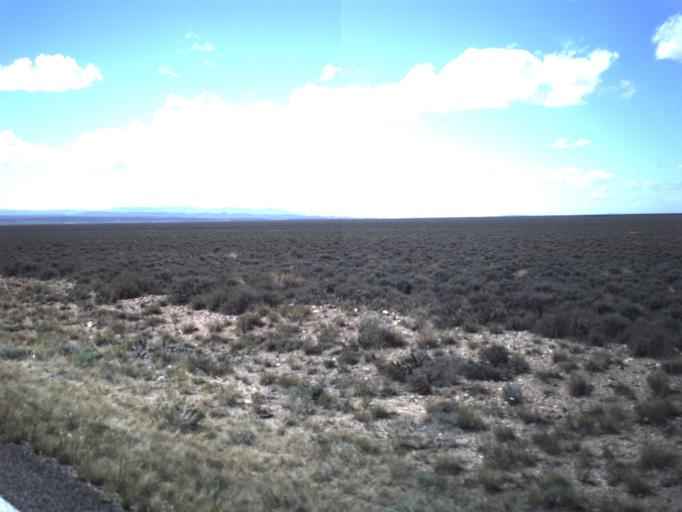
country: US
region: Utah
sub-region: Iron County
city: Enoch
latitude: 37.9481
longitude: -113.0171
